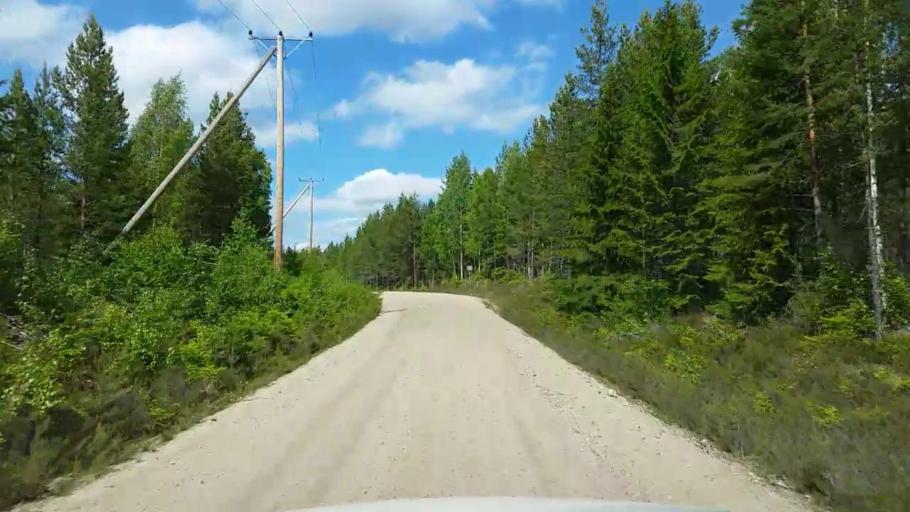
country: SE
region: Gaevleborg
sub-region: Ovanakers Kommun
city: Edsbyn
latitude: 61.5334
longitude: 15.9576
